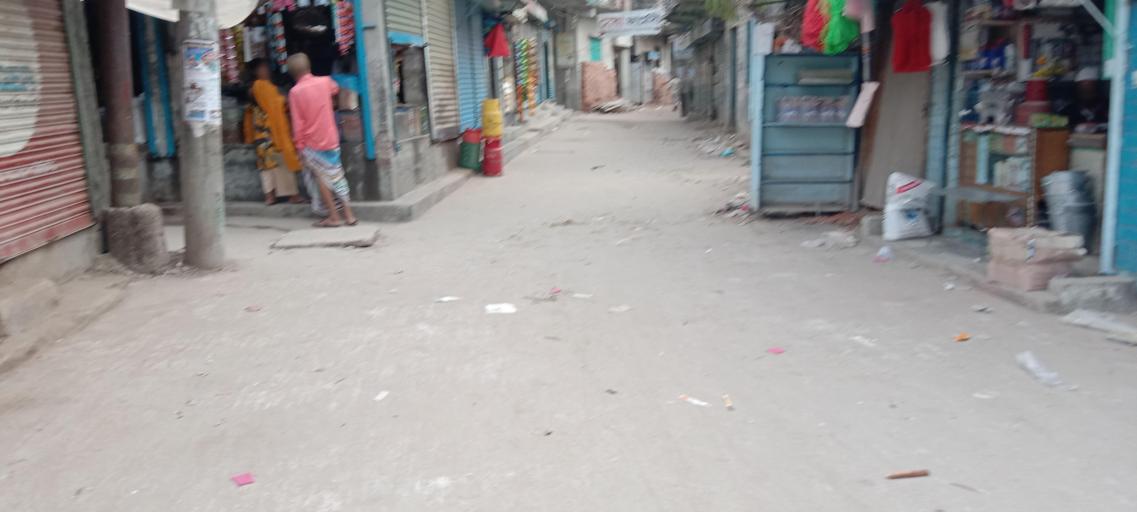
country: BD
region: Dhaka
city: Azimpur
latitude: 23.7061
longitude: 90.3752
